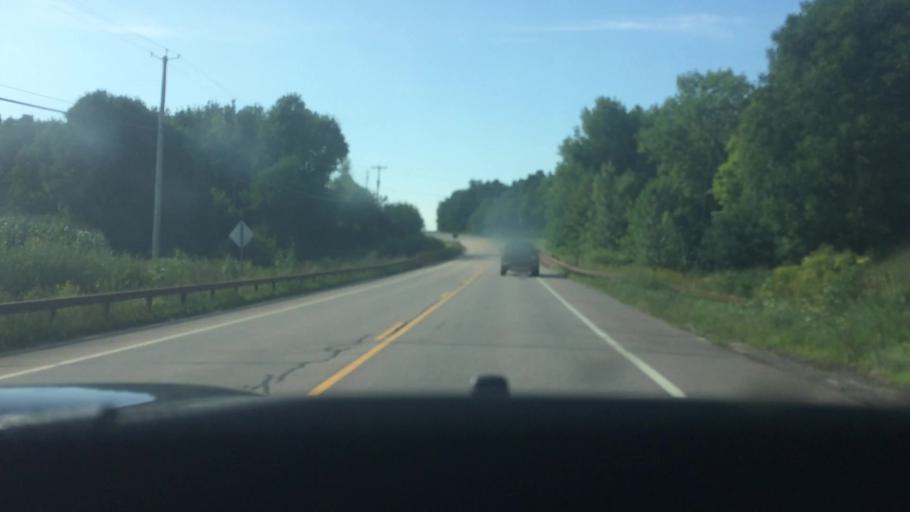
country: US
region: New York
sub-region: Franklin County
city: Malone
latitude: 44.8490
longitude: -74.1992
